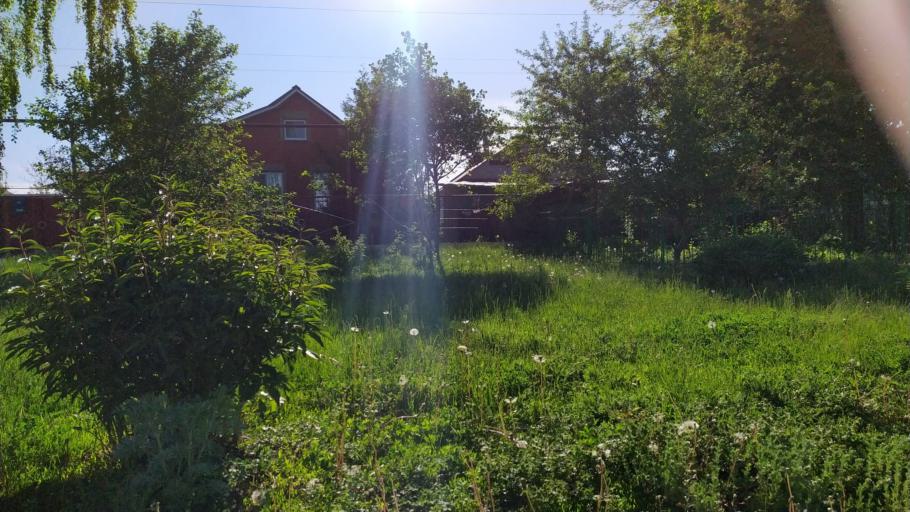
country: RU
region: Kursk
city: Kursk
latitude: 51.6351
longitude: 36.1496
